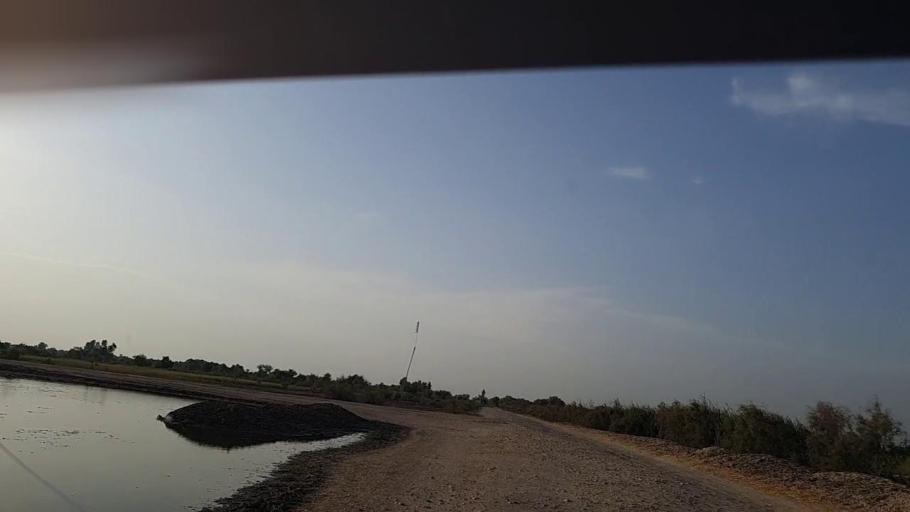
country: PK
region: Sindh
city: Khanpur
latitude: 27.8074
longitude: 69.3098
